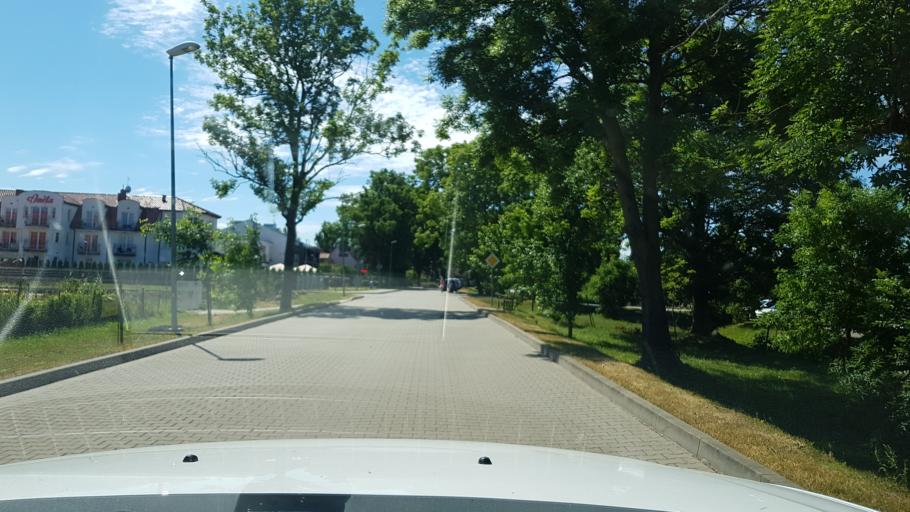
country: PL
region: West Pomeranian Voivodeship
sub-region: Powiat kolobrzeski
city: Grzybowo
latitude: 54.1623
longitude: 15.4847
